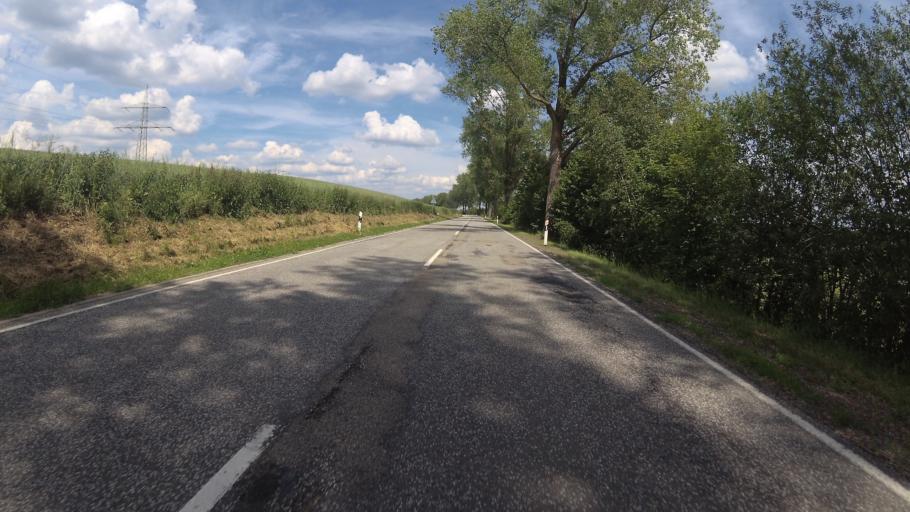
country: DE
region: Rheinland-Pfalz
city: Grossbundenbach
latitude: 49.3101
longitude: 7.3966
